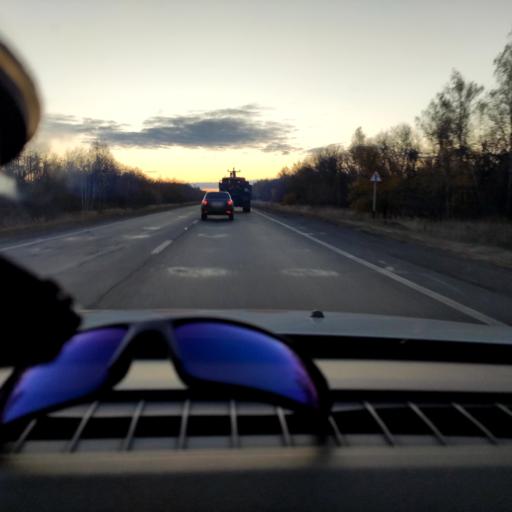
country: RU
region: Samara
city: Chapayevsk
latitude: 52.9909
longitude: 49.8428
